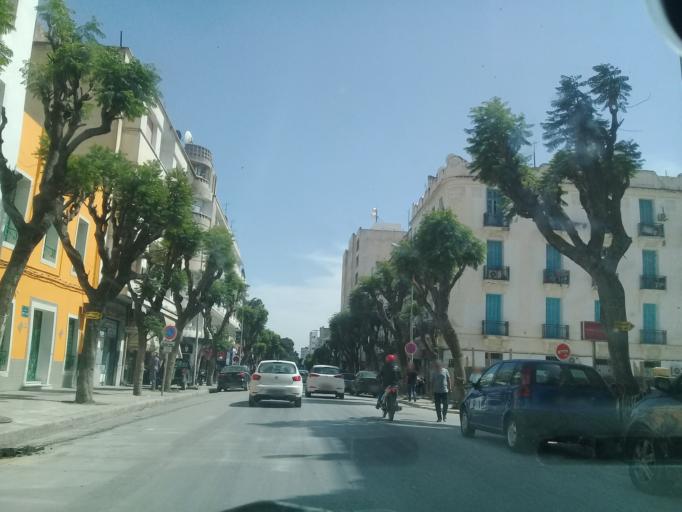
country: TN
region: Tunis
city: Tunis
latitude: 36.8101
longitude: 10.1797
